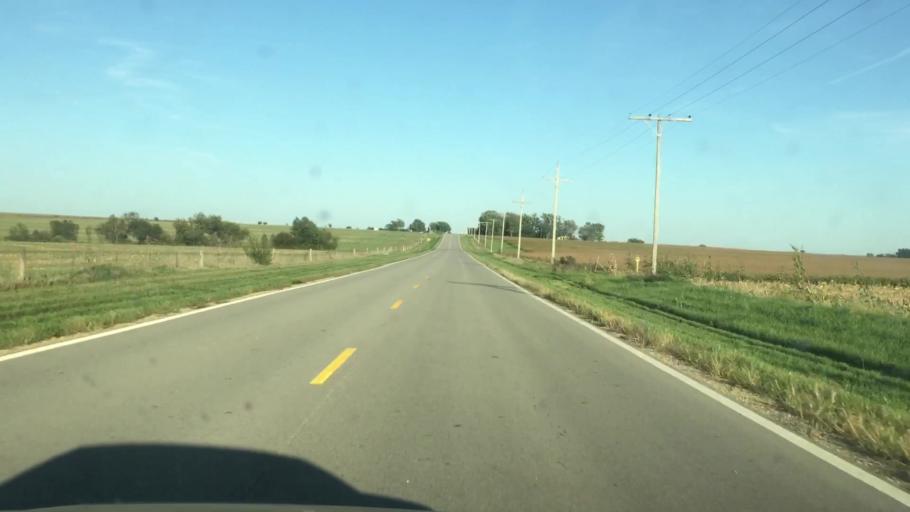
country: US
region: Kansas
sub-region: Brown County
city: Horton
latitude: 39.5876
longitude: -95.5990
